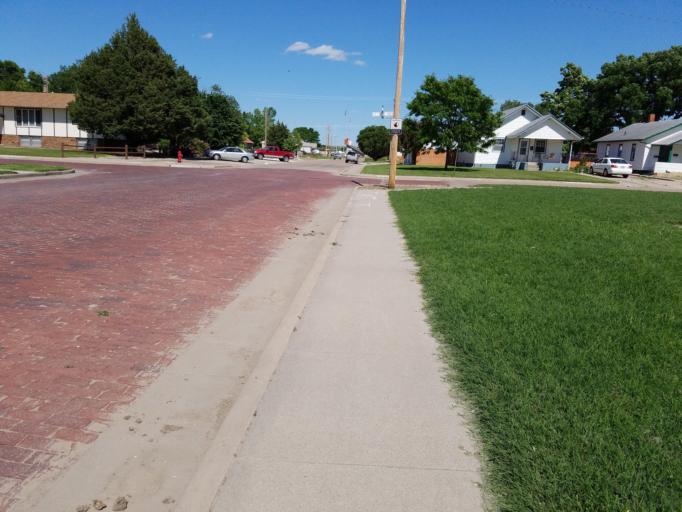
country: US
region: Kansas
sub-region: Decatur County
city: Oberlin
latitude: 39.8189
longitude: -100.5267
